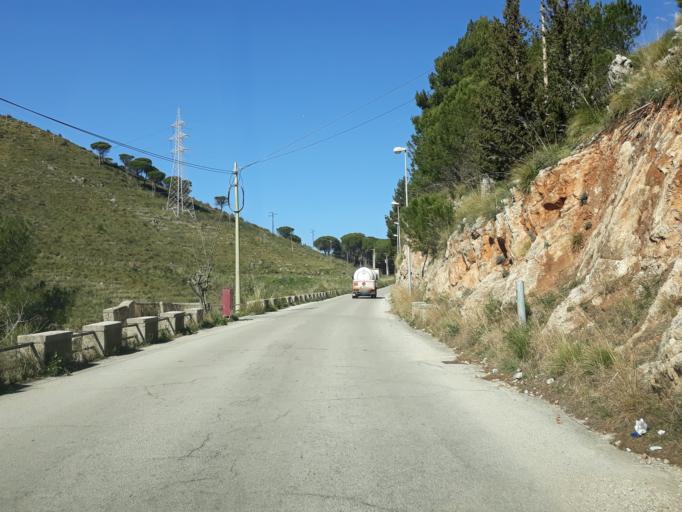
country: IT
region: Sicily
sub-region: Palermo
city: Piano dei Geli
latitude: 38.0806
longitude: 13.2735
